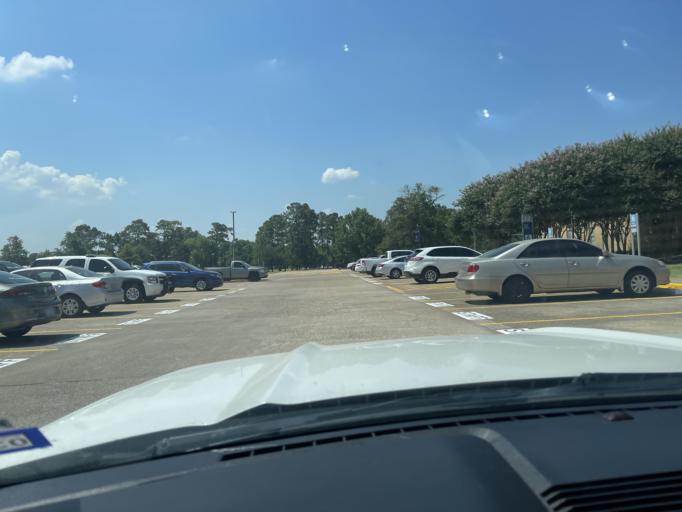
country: US
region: Texas
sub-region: Harris County
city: Cloverleaf
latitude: 29.8105
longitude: -95.1795
